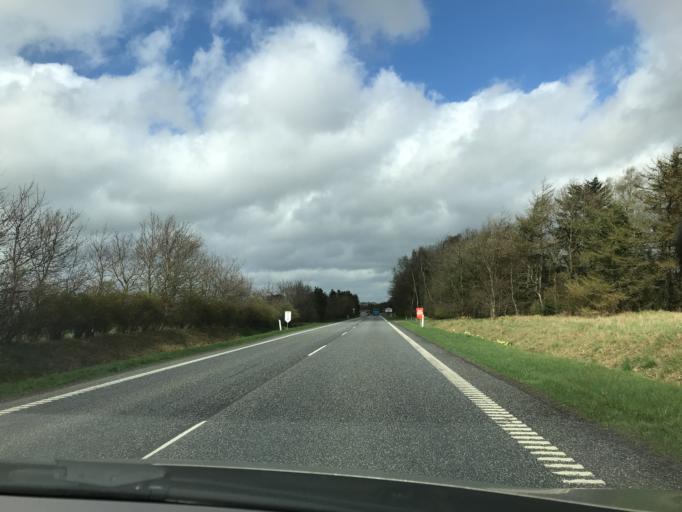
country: DK
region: Central Jutland
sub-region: Viborg Kommune
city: Stoholm
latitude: 56.4015
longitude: 9.0018
